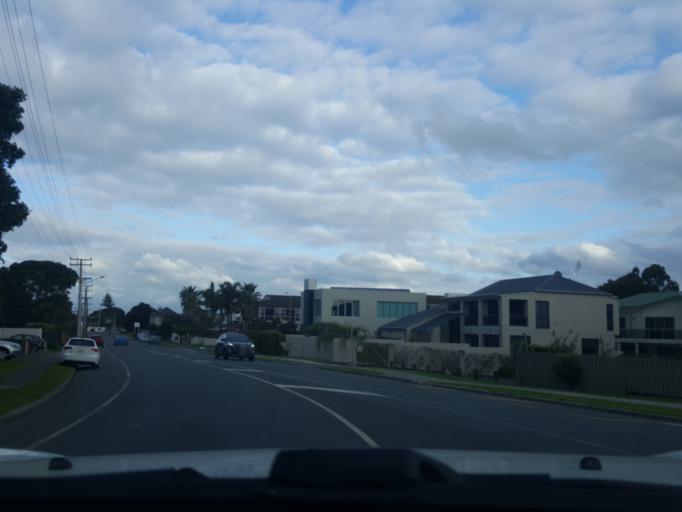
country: NZ
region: Bay of Plenty
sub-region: Tauranga City
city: Tauranga
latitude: -37.6544
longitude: 176.2076
